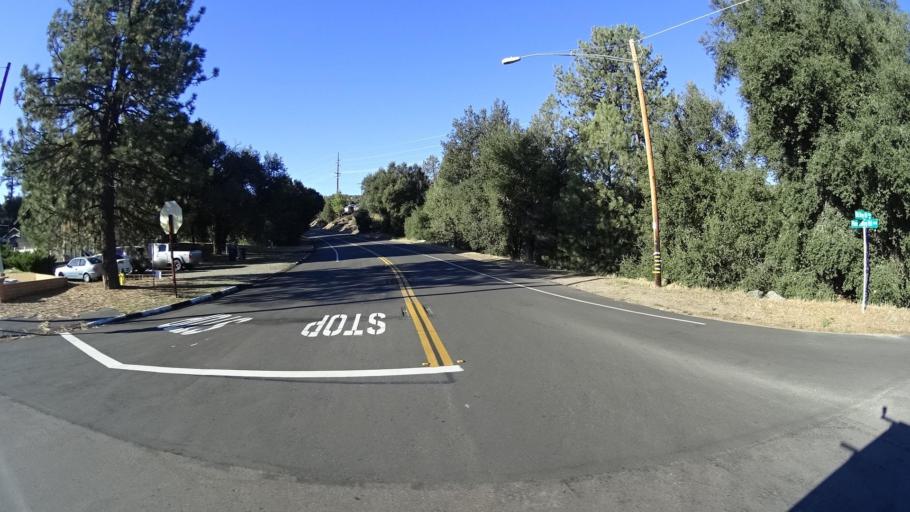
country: US
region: California
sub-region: San Diego County
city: Pine Valley
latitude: 32.8228
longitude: -116.5308
